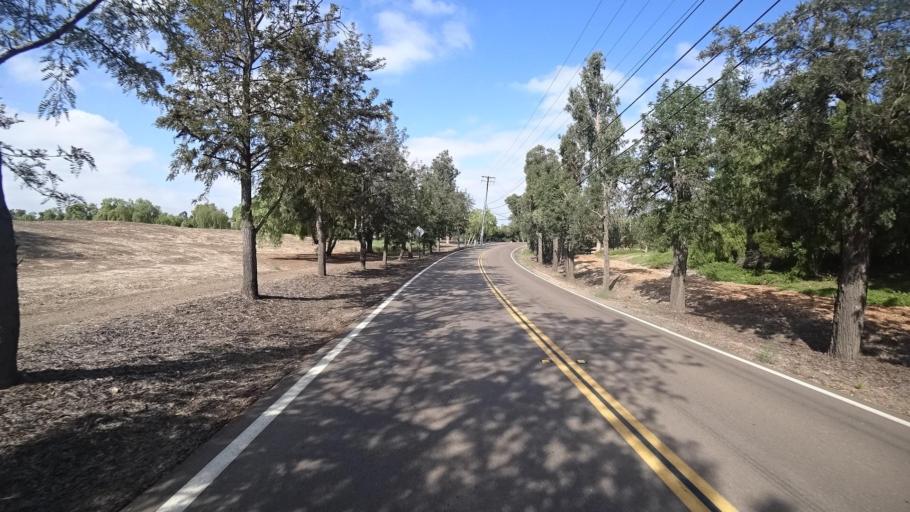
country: US
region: California
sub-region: San Diego County
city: Rancho Santa Fe
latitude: 33.0445
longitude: -117.2078
